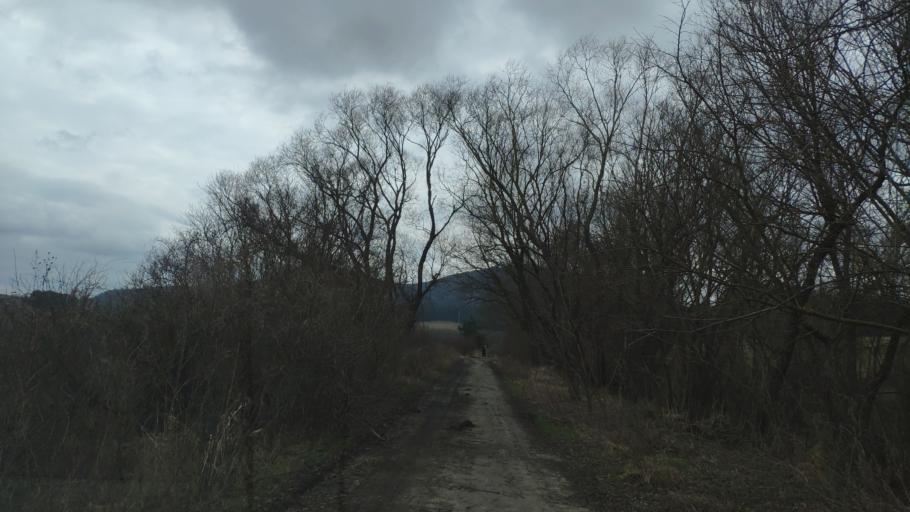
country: SK
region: Presovsky
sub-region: Okres Presov
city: Presov
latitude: 49.0829
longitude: 21.2856
